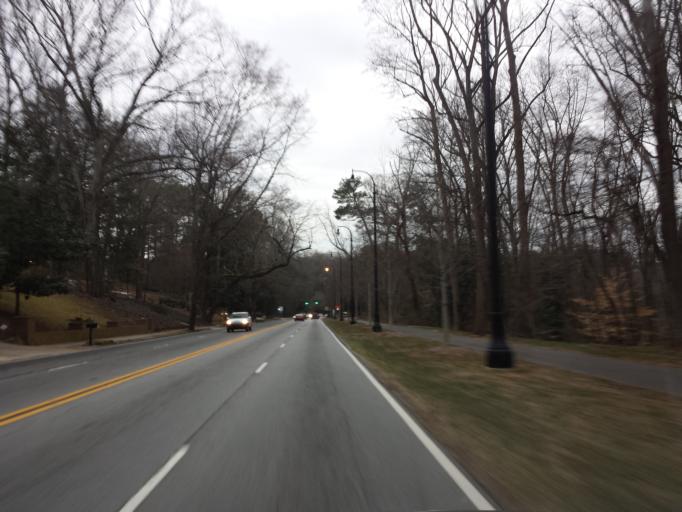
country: US
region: Georgia
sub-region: DeKalb County
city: Druid Hills
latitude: 33.7718
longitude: -84.3225
